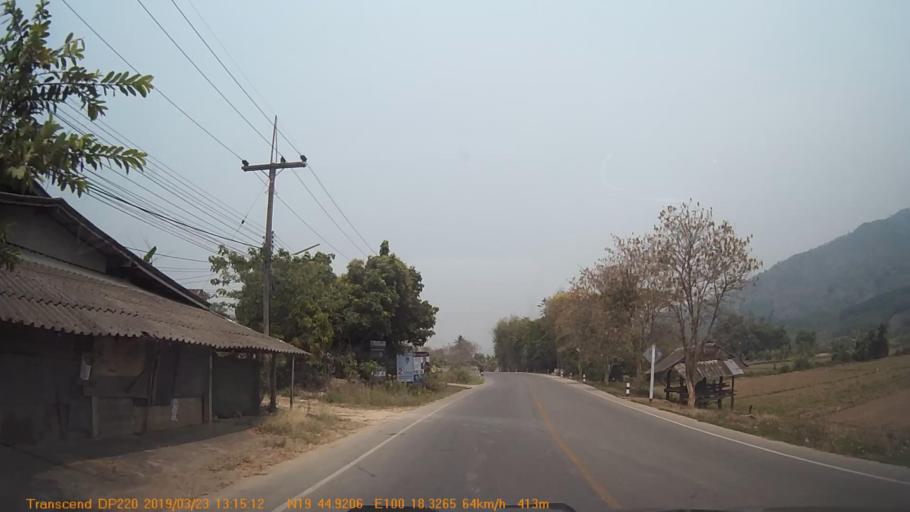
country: TH
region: Chiang Rai
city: Khun Tan
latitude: 19.7488
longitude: 100.3055
